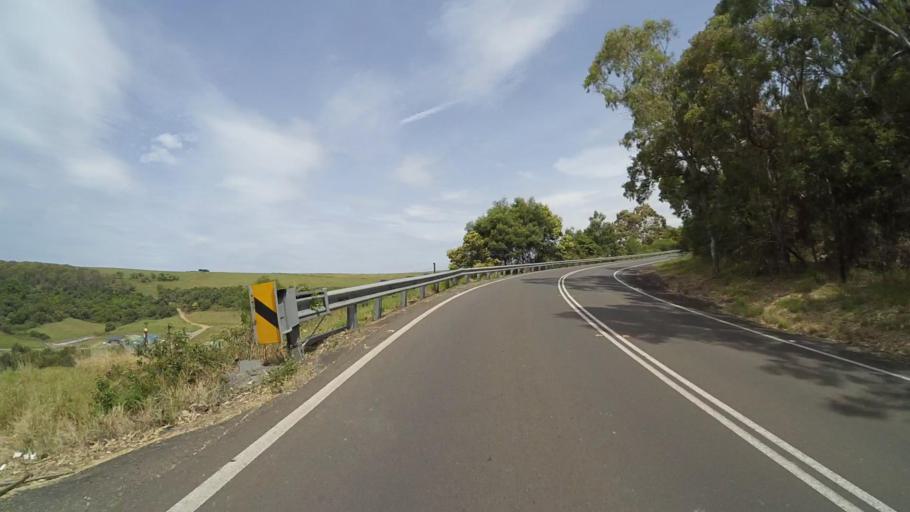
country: AU
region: New South Wales
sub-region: Shellharbour
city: Albion Park Rail
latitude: -34.5965
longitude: 150.7856
